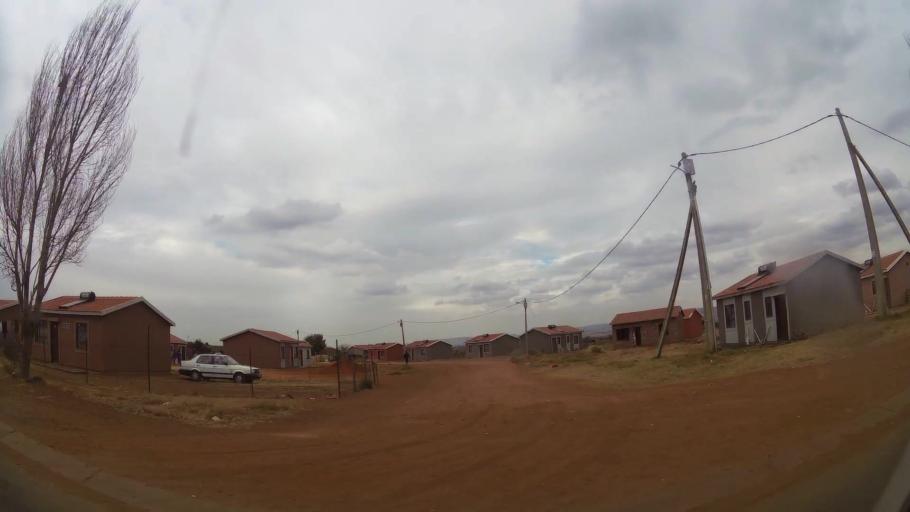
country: ZA
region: Gauteng
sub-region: Ekurhuleni Metropolitan Municipality
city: Germiston
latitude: -26.3962
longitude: 28.1512
